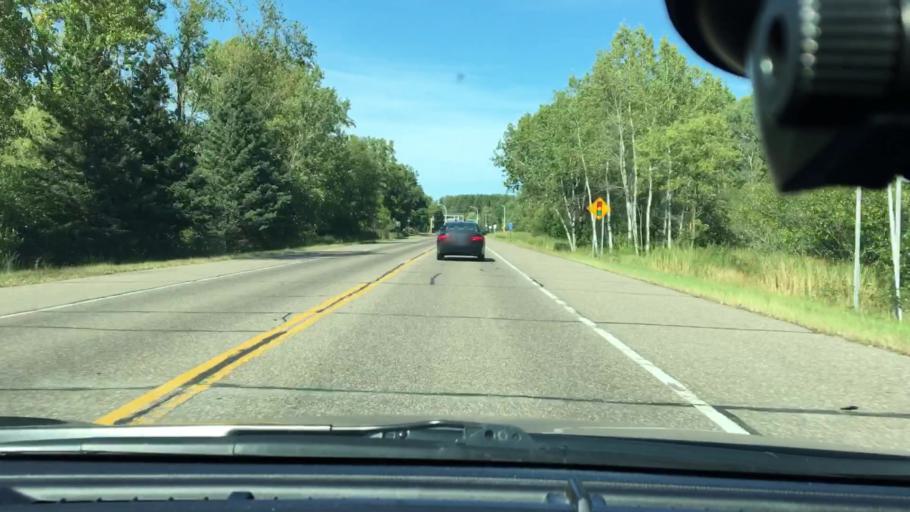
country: US
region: Minnesota
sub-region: Washington County
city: Mahtomedi
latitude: 45.0538
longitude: -92.9475
